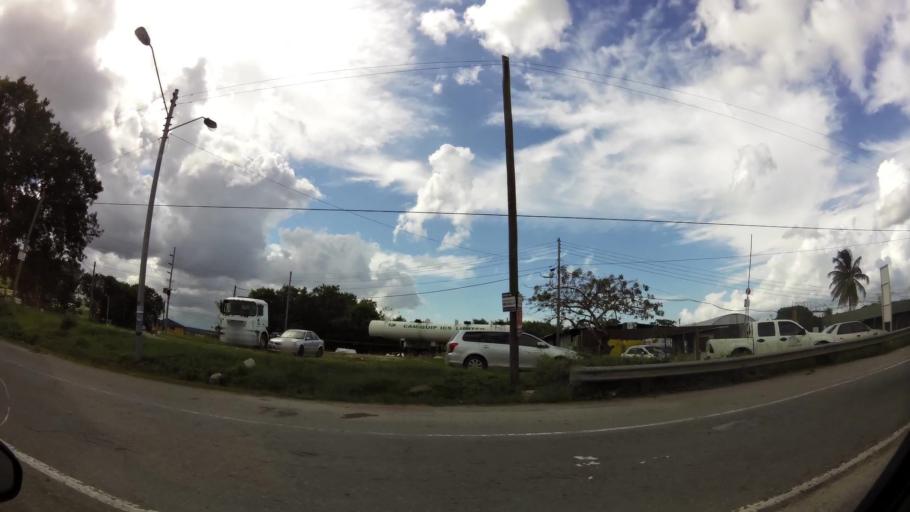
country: TT
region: City of San Fernando
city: Mon Repos
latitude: 10.2598
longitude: -61.4552
